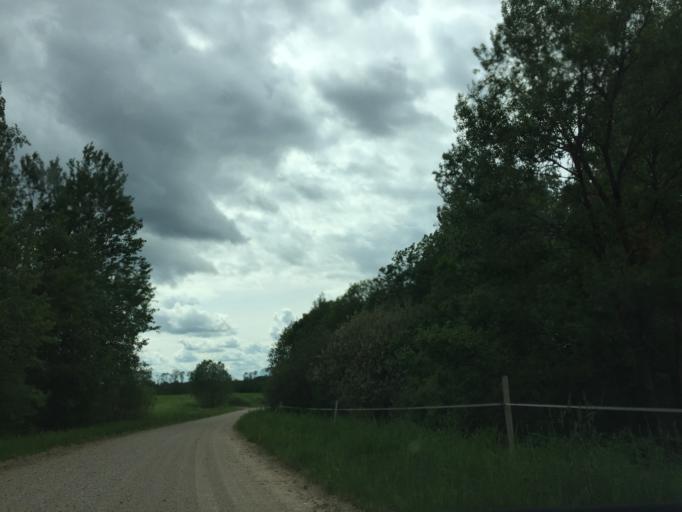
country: LV
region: Dagda
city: Dagda
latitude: 56.0713
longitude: 27.6607
